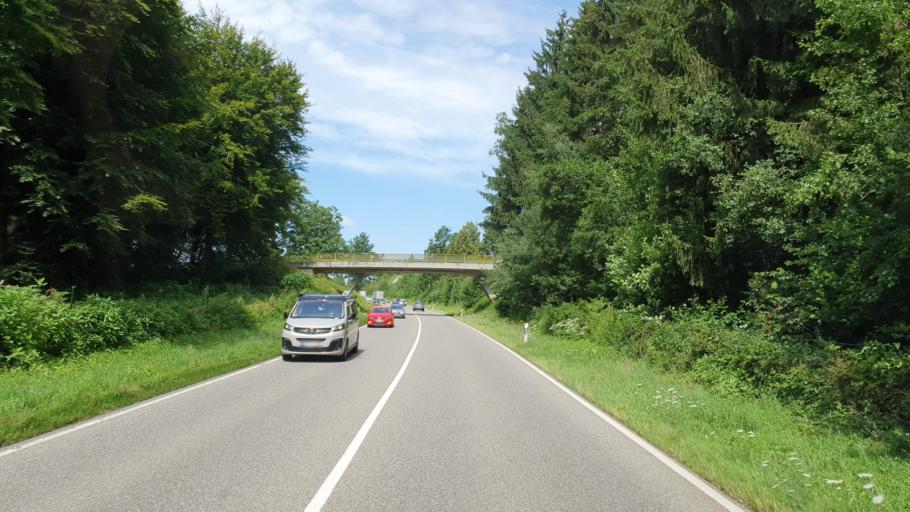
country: DE
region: Bavaria
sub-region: Swabia
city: Nonnenhorn
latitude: 47.5936
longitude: 9.6404
